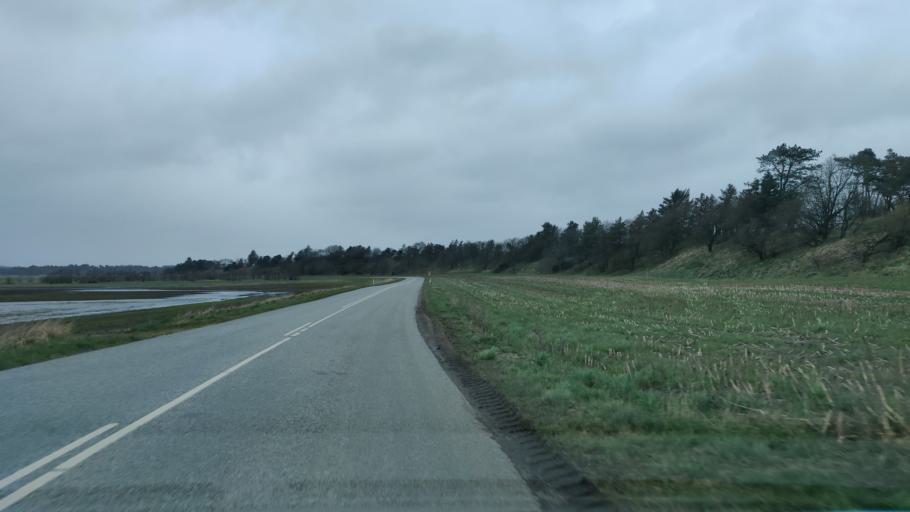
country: DK
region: Central Jutland
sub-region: Skive Kommune
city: Hojslev
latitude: 56.5617
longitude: 9.2485
